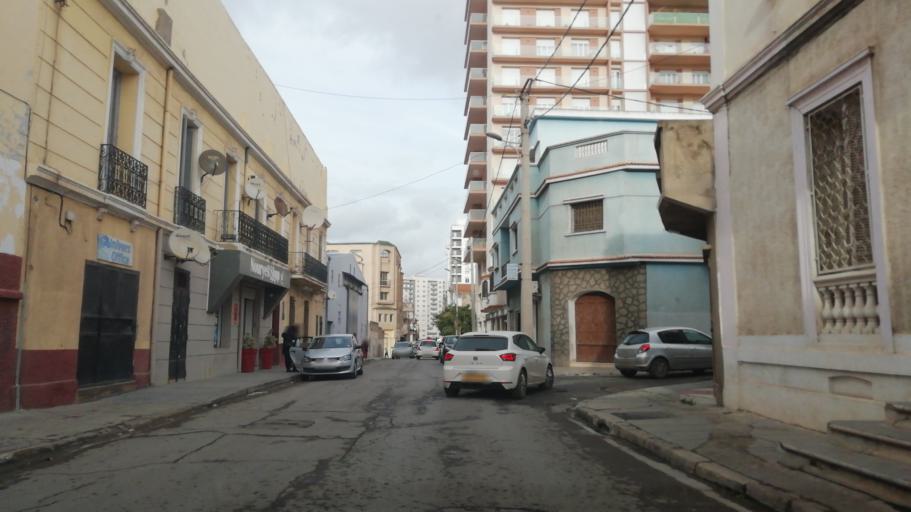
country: DZ
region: Oran
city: Oran
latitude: 35.7015
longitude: -0.6241
